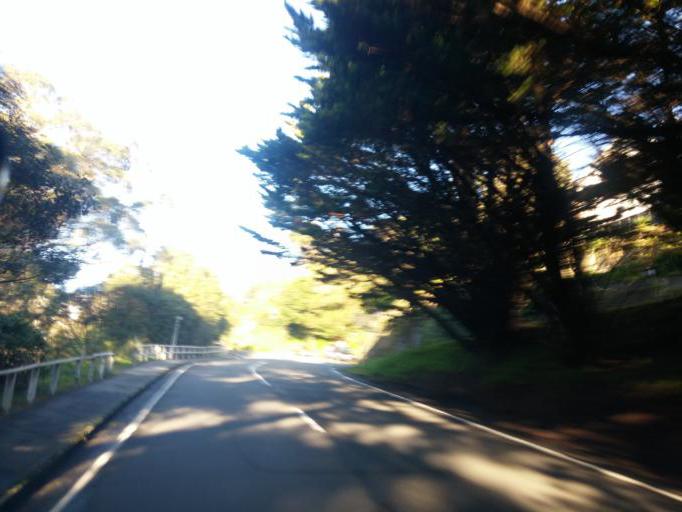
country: NZ
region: Wellington
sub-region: Wellington City
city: Kelburn
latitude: -41.3008
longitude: 174.7650
